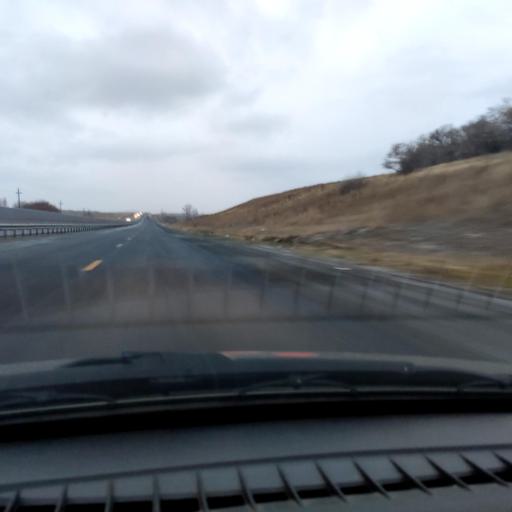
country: RU
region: Samara
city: Kurumoch
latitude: 53.4996
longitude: 50.0278
